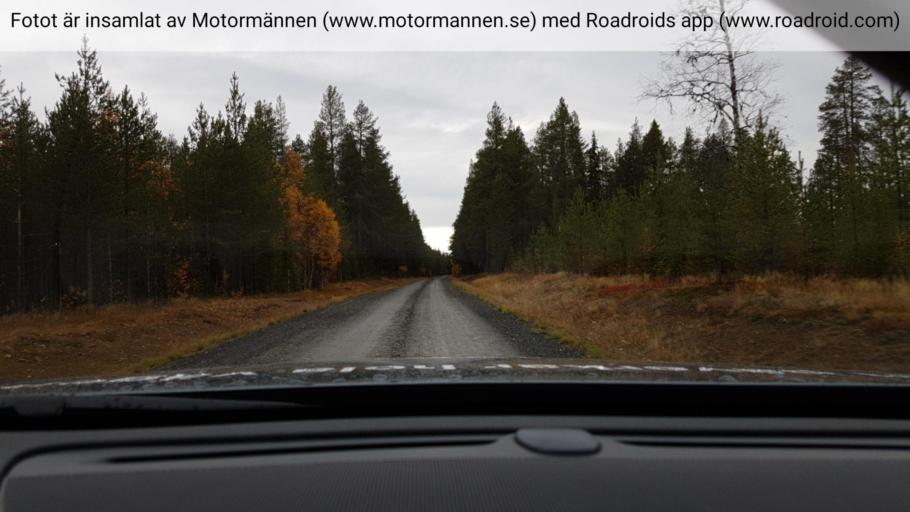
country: SE
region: Norrbotten
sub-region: Pajala Kommun
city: Pajala
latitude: 67.1257
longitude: 22.6721
